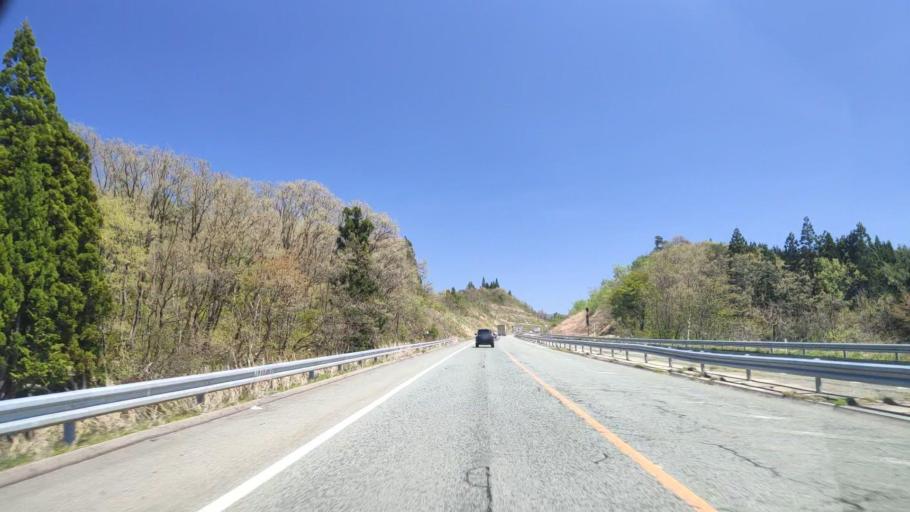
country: JP
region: Yamagata
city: Obanazawa
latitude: 38.6666
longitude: 140.3450
